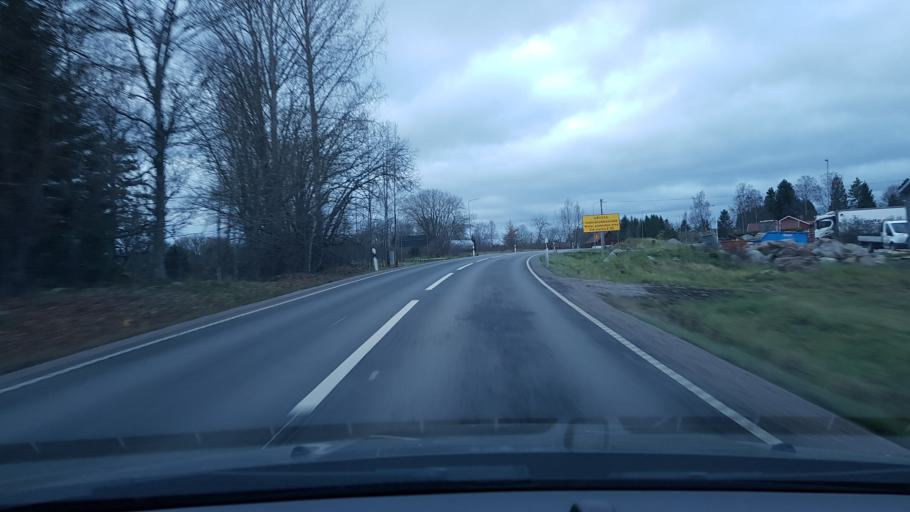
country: SE
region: Uppsala
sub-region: Uppsala Kommun
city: Vattholma
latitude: 59.9512
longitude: 17.9010
